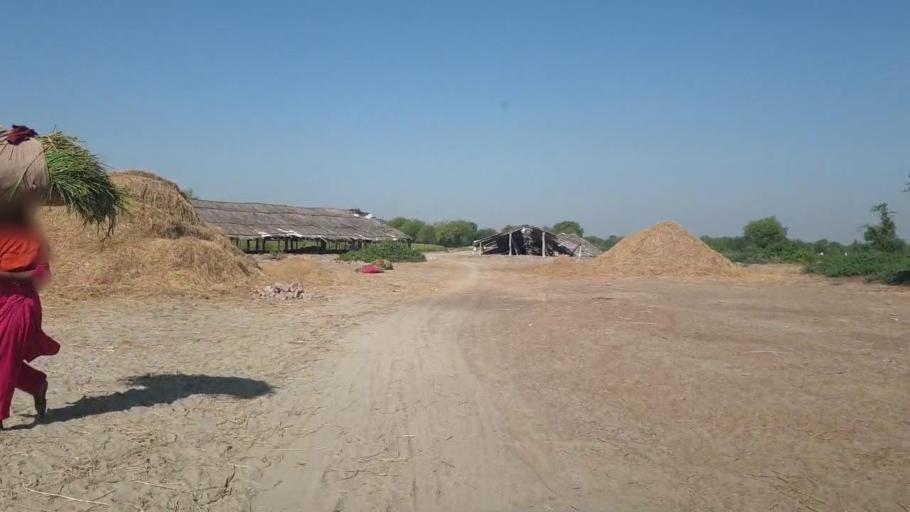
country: PK
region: Sindh
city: Talhar
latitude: 24.8122
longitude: 68.7858
